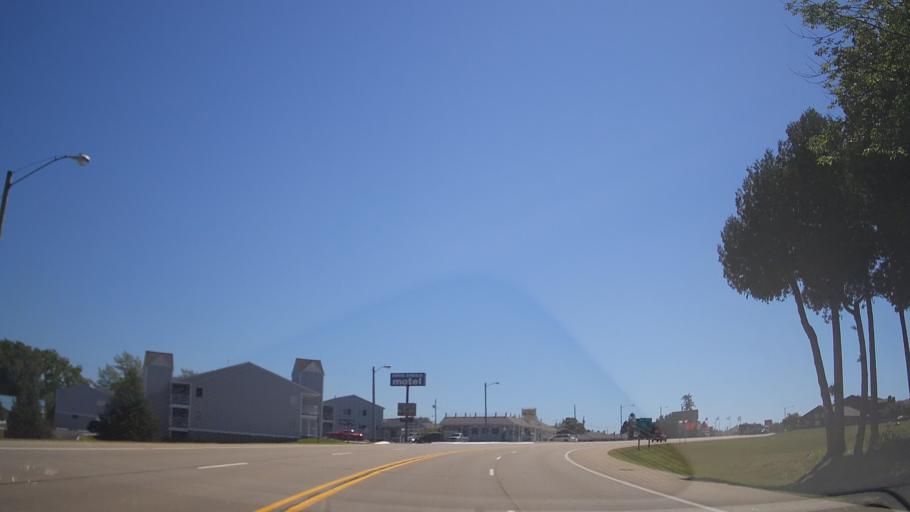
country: US
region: Michigan
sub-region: Mackinac County
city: Saint Ignace
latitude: 45.8606
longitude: -84.7161
